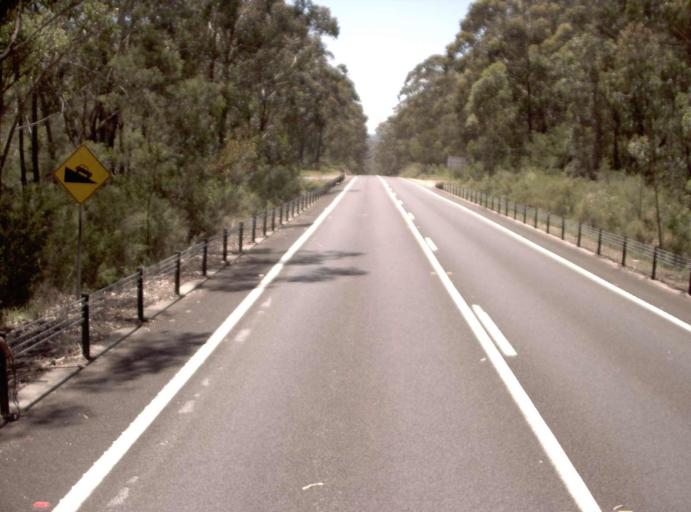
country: AU
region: Victoria
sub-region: East Gippsland
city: Lakes Entrance
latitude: -37.7475
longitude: 148.0714
